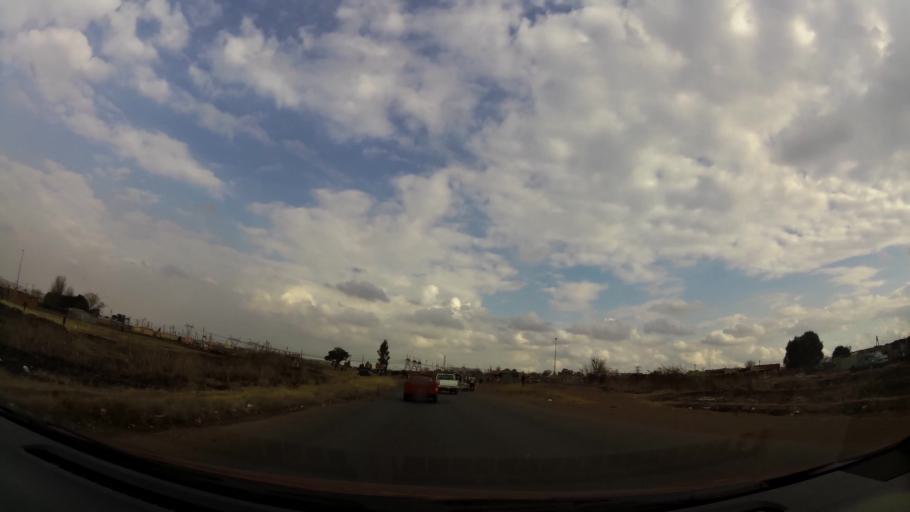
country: ZA
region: Gauteng
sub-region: Sedibeng District Municipality
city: Vanderbijlpark
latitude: -26.6742
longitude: 27.8594
